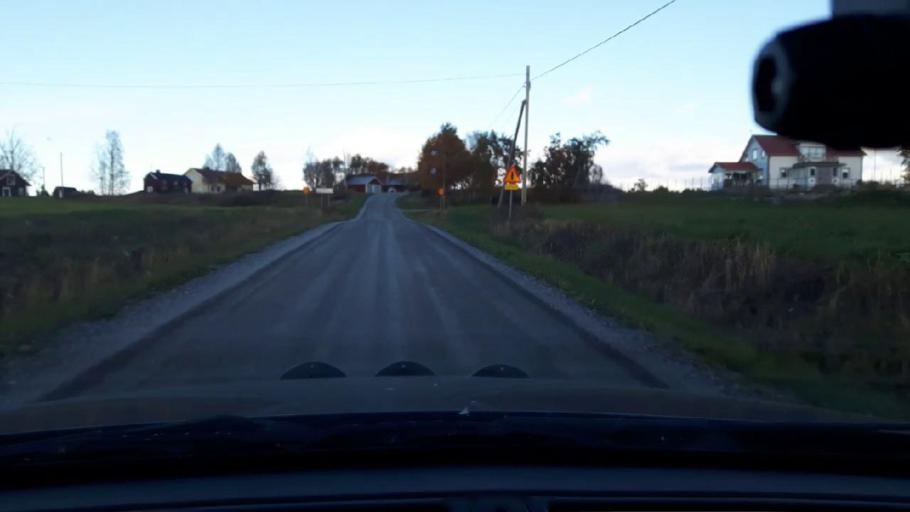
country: SE
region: Jaemtland
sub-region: Krokoms Kommun
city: Krokom
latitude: 63.0785
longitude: 14.2748
